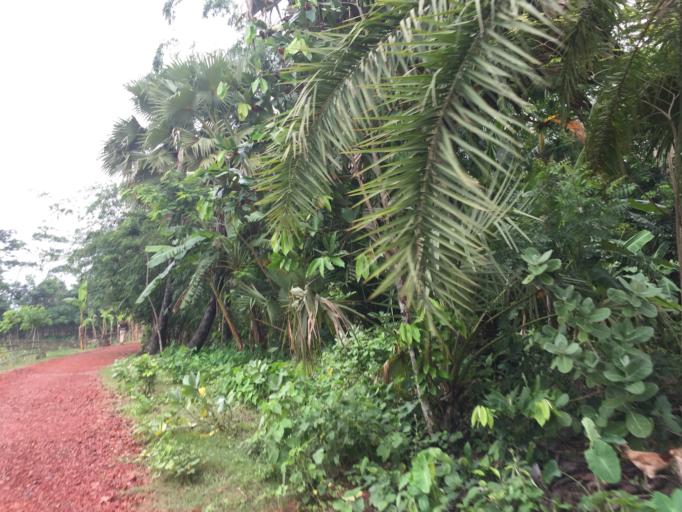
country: BD
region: Barisal
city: Mathba
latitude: 22.1986
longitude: 89.9350
